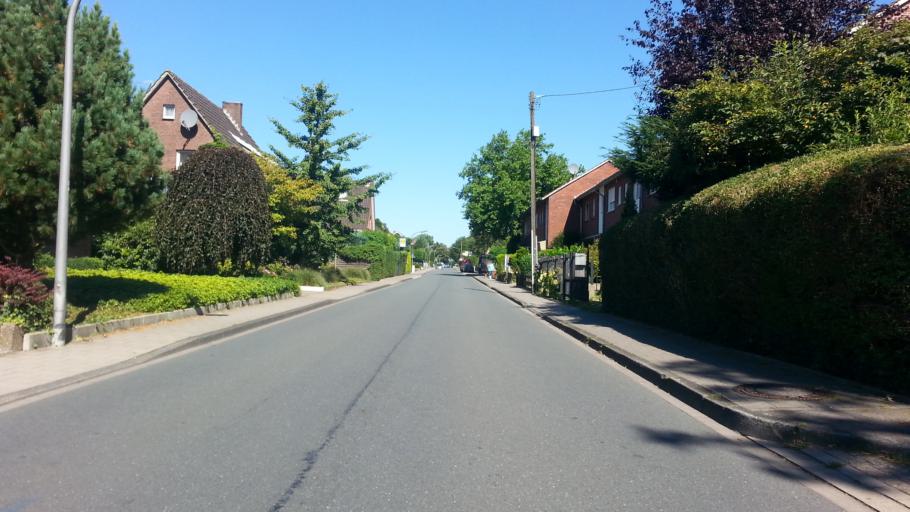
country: DE
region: North Rhine-Westphalia
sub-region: Regierungsbezirk Munster
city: Muenster
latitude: 51.9506
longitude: 7.5374
